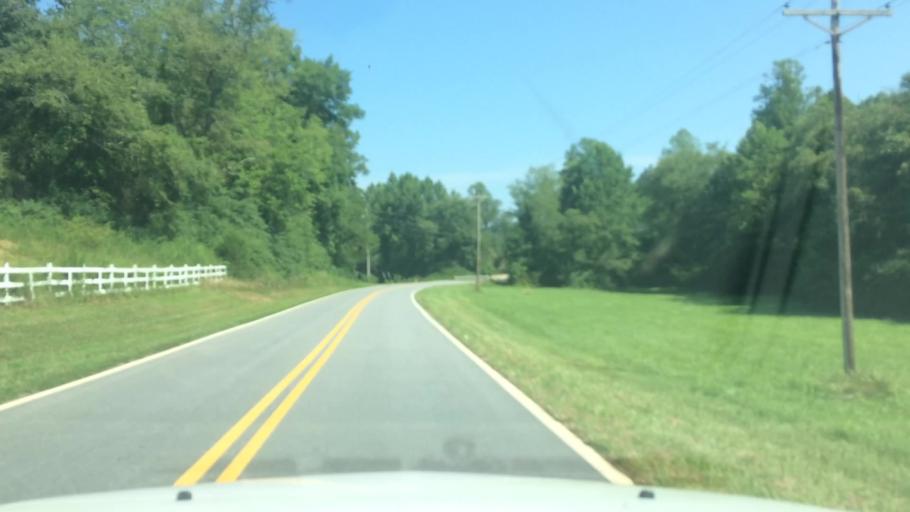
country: US
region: North Carolina
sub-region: Alexander County
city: Taylorsville
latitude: 35.9576
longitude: -81.2691
